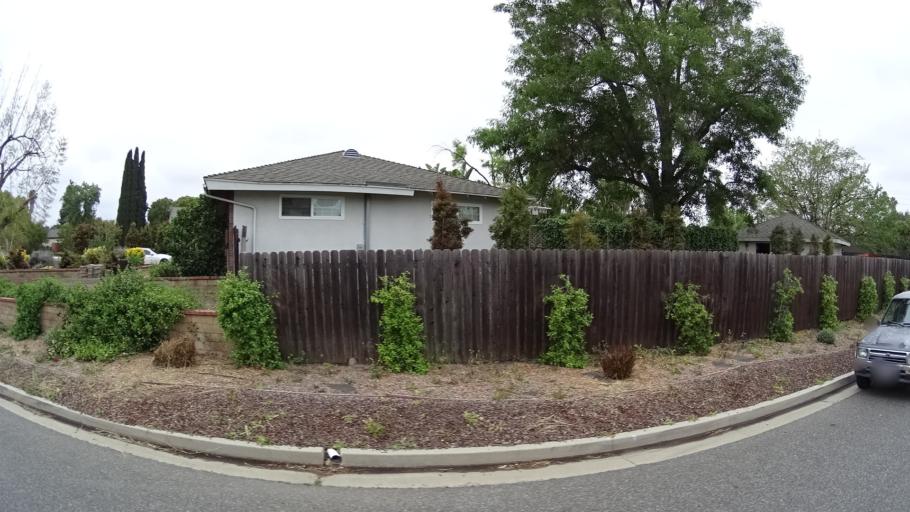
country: US
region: California
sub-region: Ventura County
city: Thousand Oaks
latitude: 34.2054
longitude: -118.8666
